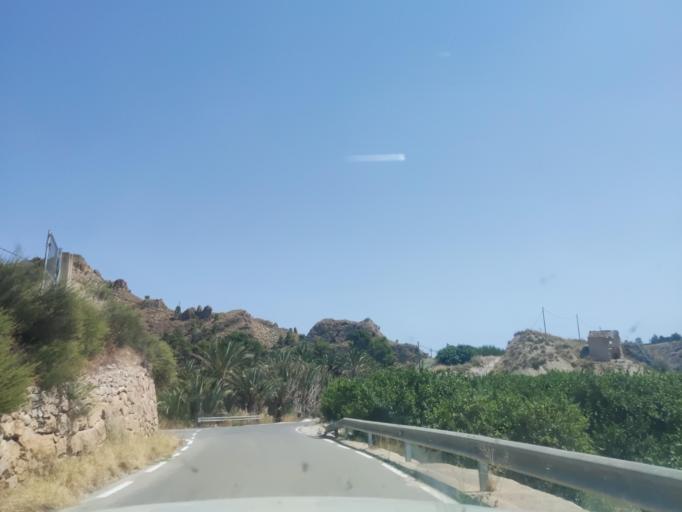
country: ES
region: Murcia
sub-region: Murcia
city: Ulea
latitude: 38.1332
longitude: -1.3146
